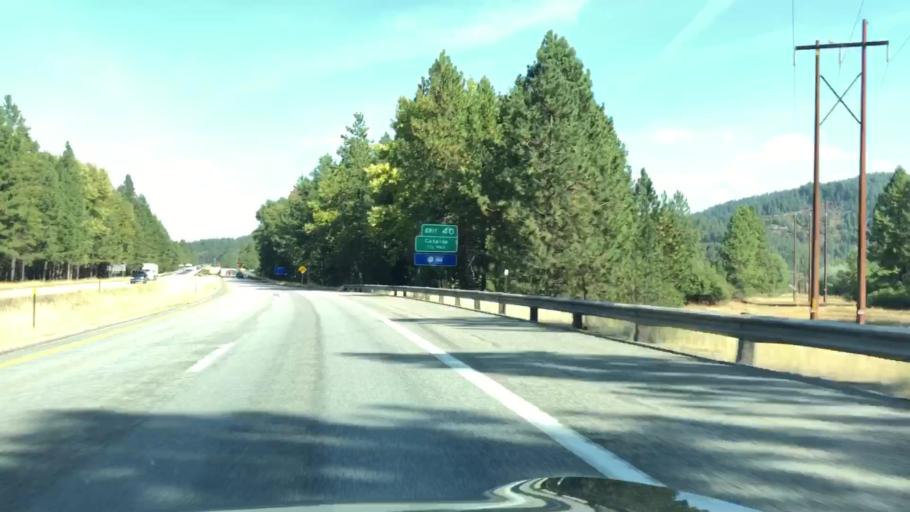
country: US
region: Idaho
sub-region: Shoshone County
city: Pinehurst
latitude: 47.5460
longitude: -116.3409
